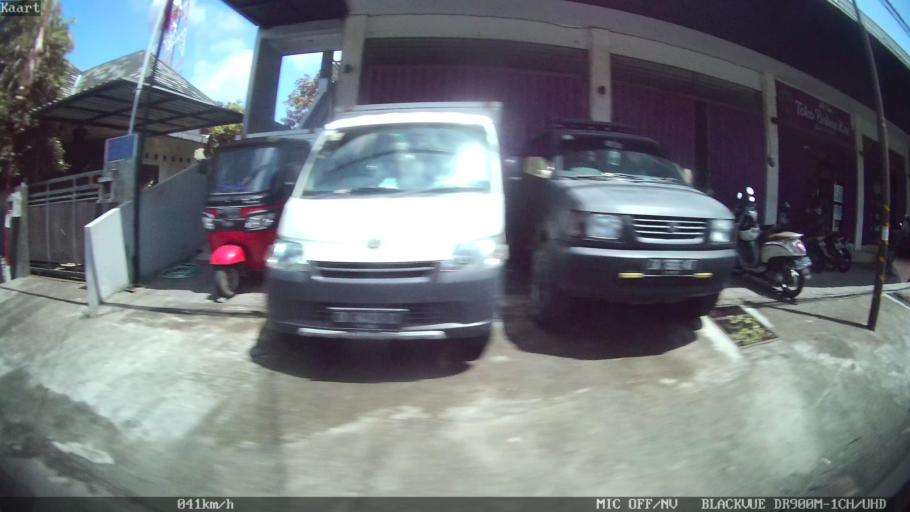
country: ID
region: Bali
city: Banjar Jabejero
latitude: -8.6044
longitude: 115.2588
